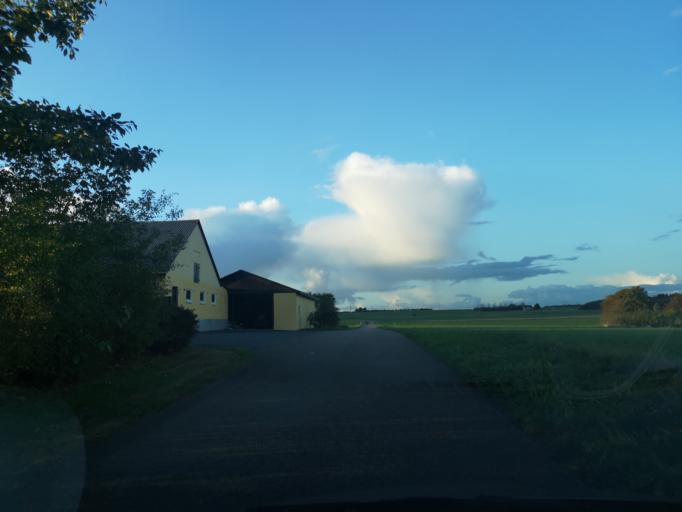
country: DK
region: Central Jutland
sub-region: Ringkobing-Skjern Kommune
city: Videbaek
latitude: 56.0427
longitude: 8.5809
